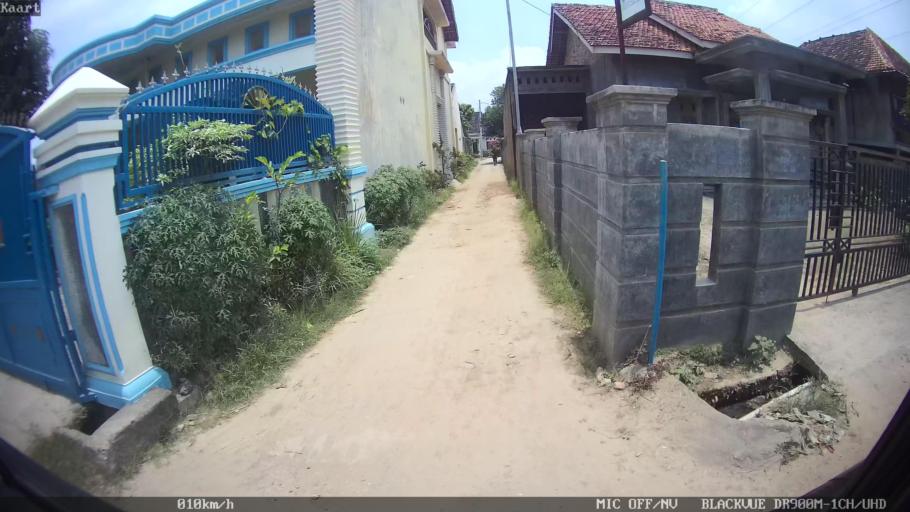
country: ID
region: Lampung
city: Kedaton
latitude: -5.3349
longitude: 105.2472
